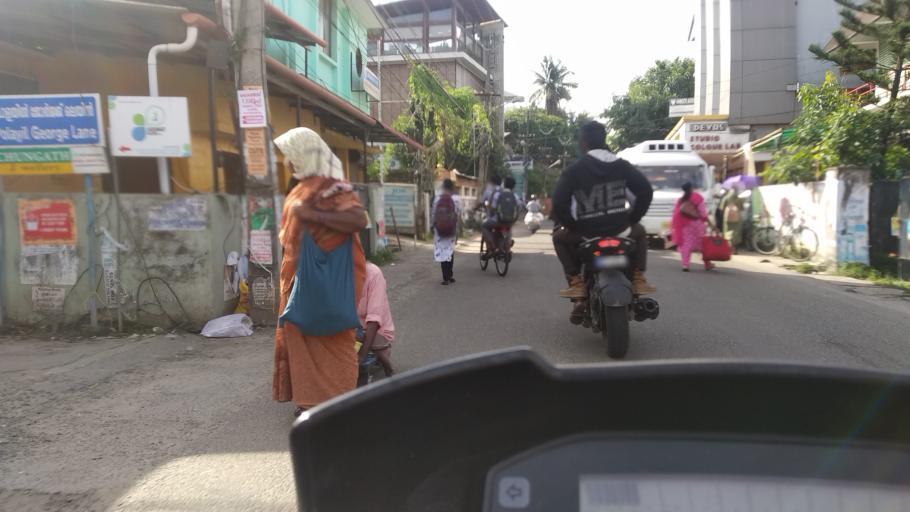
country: IN
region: Kerala
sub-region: Ernakulam
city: Elur
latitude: 9.9991
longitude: 76.2965
